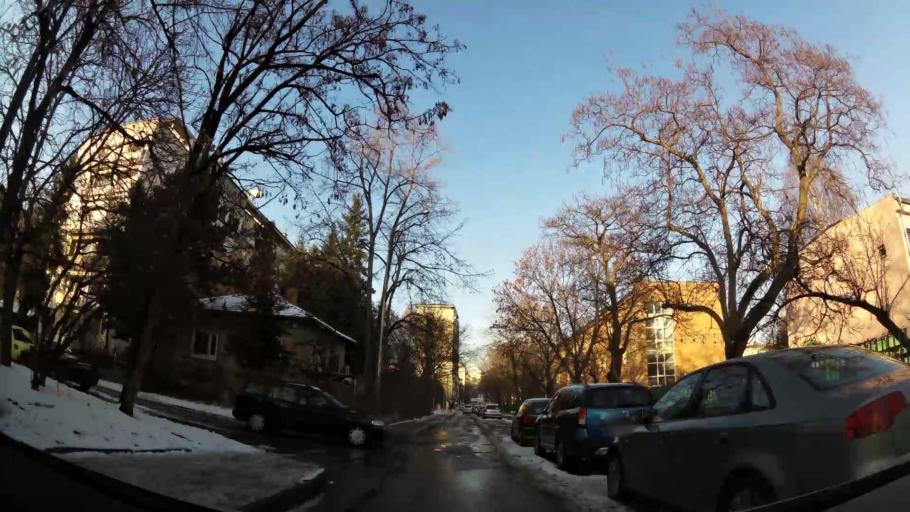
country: BG
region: Sofia-Capital
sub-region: Stolichna Obshtina
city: Sofia
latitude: 42.6822
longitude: 23.3615
